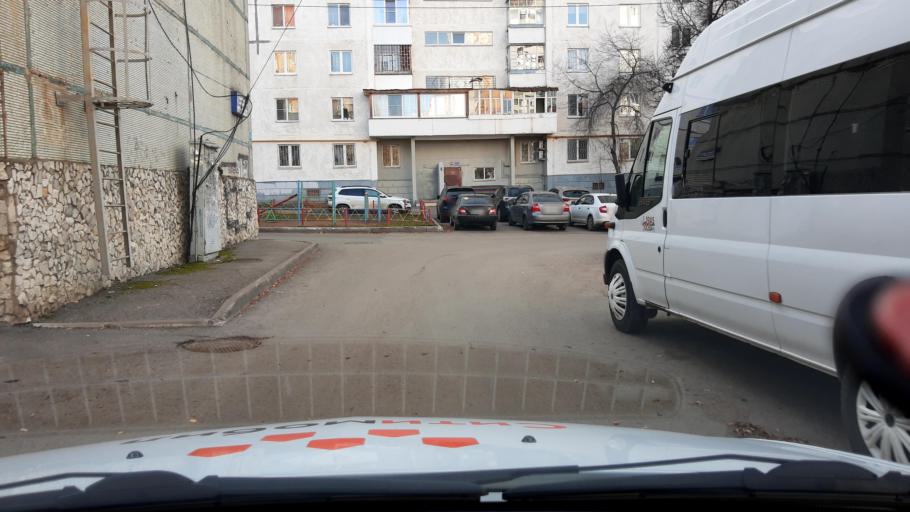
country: RU
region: Bashkortostan
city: Ufa
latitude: 54.7174
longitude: 56.0121
